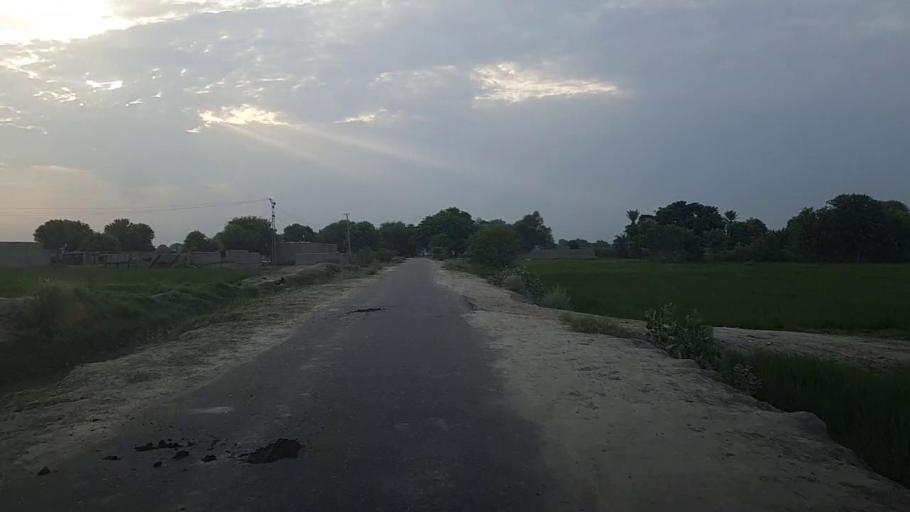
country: PK
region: Sindh
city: Ubauro
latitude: 28.3599
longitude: 69.7845
